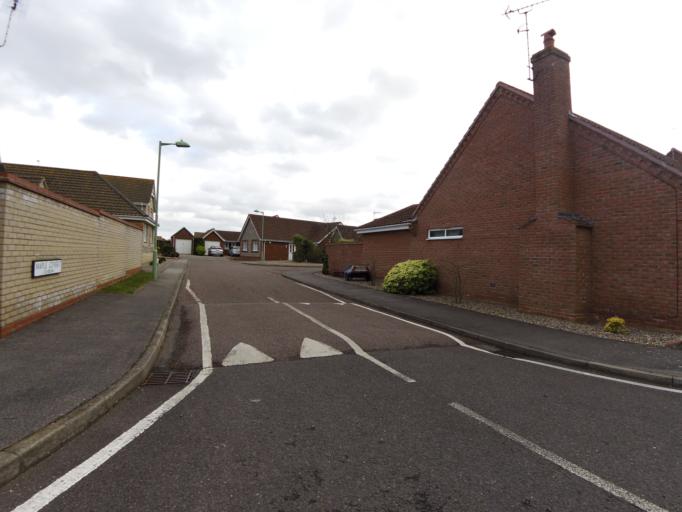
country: GB
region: England
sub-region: Norfolk
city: Hopton on Sea
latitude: 52.5003
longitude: 1.7251
